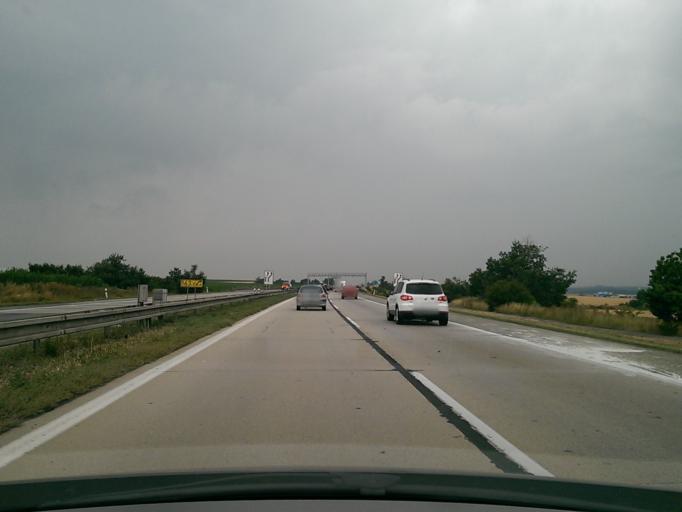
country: CZ
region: Vysocina
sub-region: Okres Zd'ar nad Sazavou
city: Velka Bites
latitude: 49.2728
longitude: 16.2374
